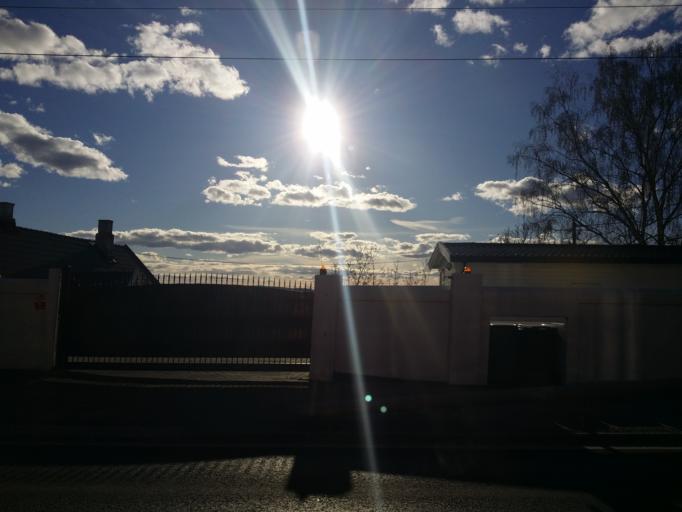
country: NO
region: Akershus
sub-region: Oppegard
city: Kolbotn
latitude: 59.8630
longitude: 10.7845
